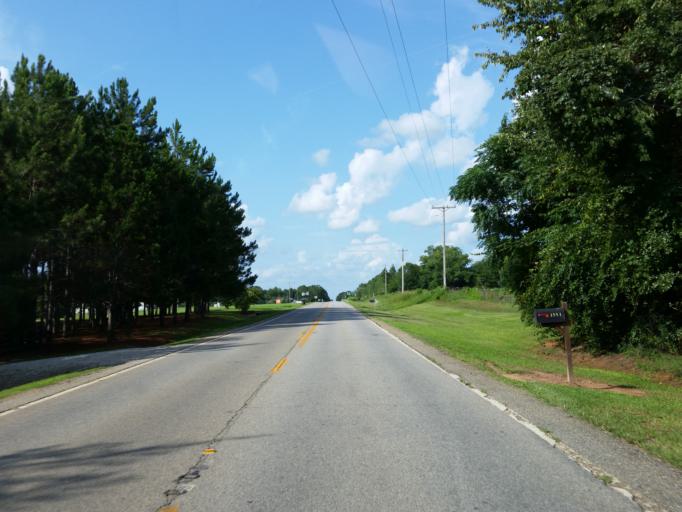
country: US
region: Georgia
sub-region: Lee County
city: Leesburg
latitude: 31.8174
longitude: -84.1115
